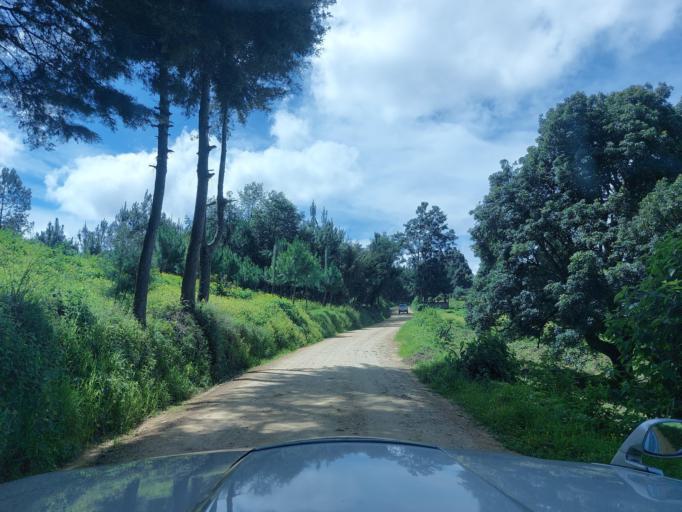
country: GT
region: Chimaltenango
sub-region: Municipio de San Juan Comalapa
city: Comalapa
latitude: 14.7592
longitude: -90.8786
